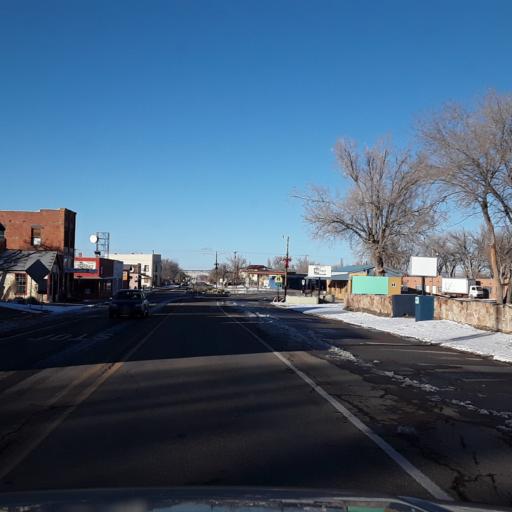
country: US
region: New Mexico
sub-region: Lincoln County
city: Carrizozo
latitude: 33.6404
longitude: -105.8780
